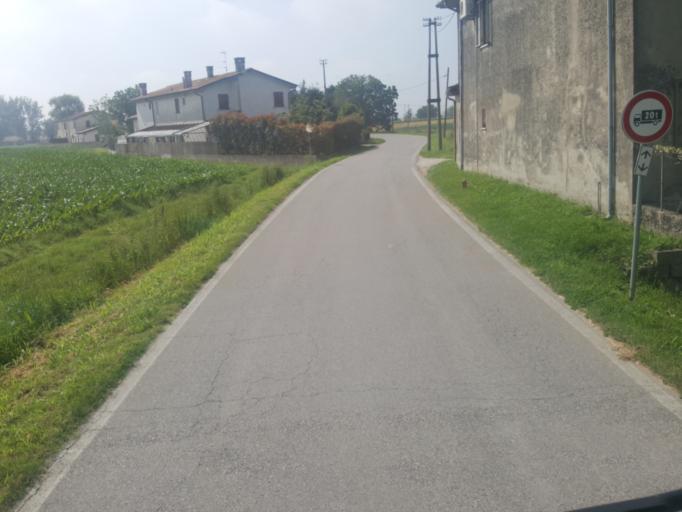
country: IT
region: Veneto
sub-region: Provincia di Rovigo
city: Canaro
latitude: 44.9379
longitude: 11.6485
